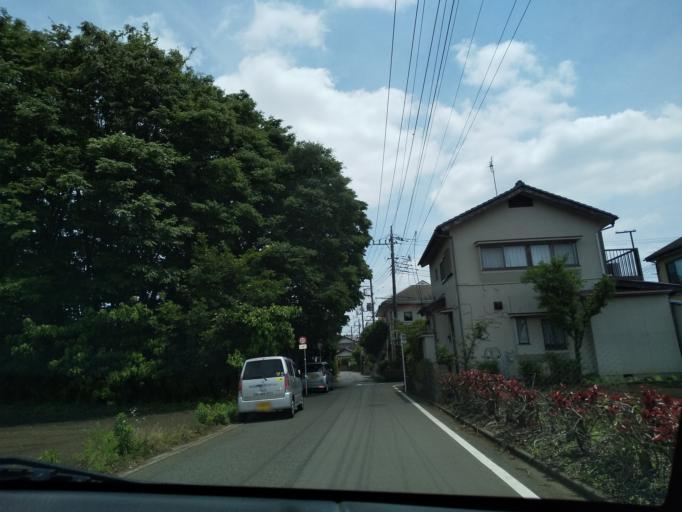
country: JP
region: Tokyo
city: Hachioji
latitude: 35.5773
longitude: 139.3255
